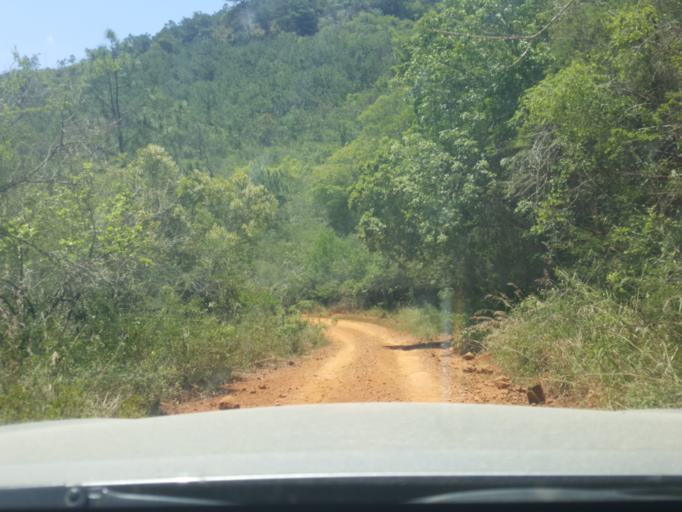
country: ZA
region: Limpopo
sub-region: Mopani District Municipality
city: Hoedspruit
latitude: -24.5918
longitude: 30.8370
